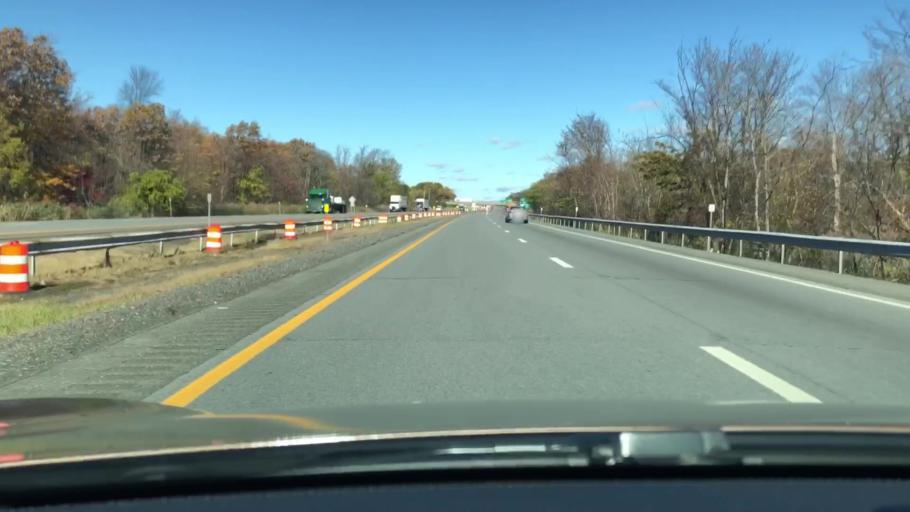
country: US
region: New York
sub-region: Orange County
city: Gardnertown
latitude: 41.5000
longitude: -74.0769
